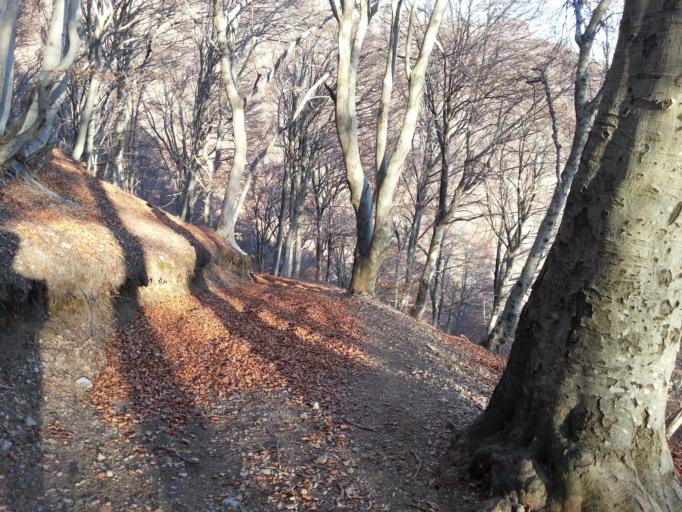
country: CH
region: Ticino
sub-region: Lugano District
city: Pregassona
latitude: 46.0201
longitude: 8.9947
